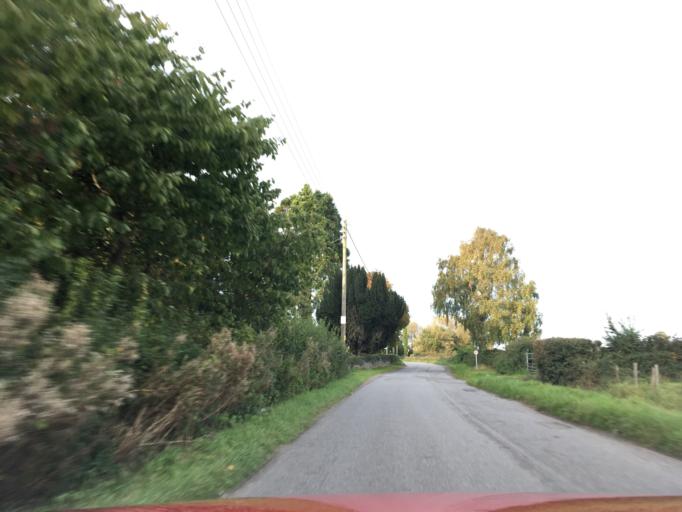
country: GB
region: England
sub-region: South Gloucestershire
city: Severn Beach
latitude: 51.5740
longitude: -2.6350
